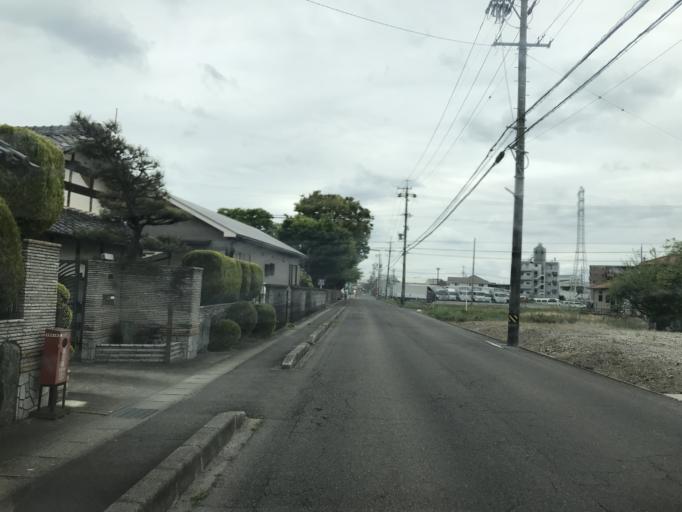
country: JP
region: Aichi
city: Kasugai
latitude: 35.2646
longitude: 136.9691
